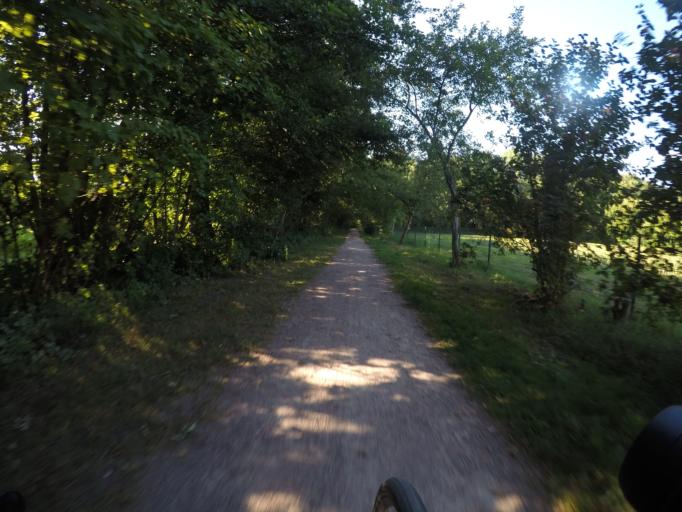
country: DE
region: Schleswig-Holstein
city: Oststeinbek
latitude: 53.5392
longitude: 10.1527
